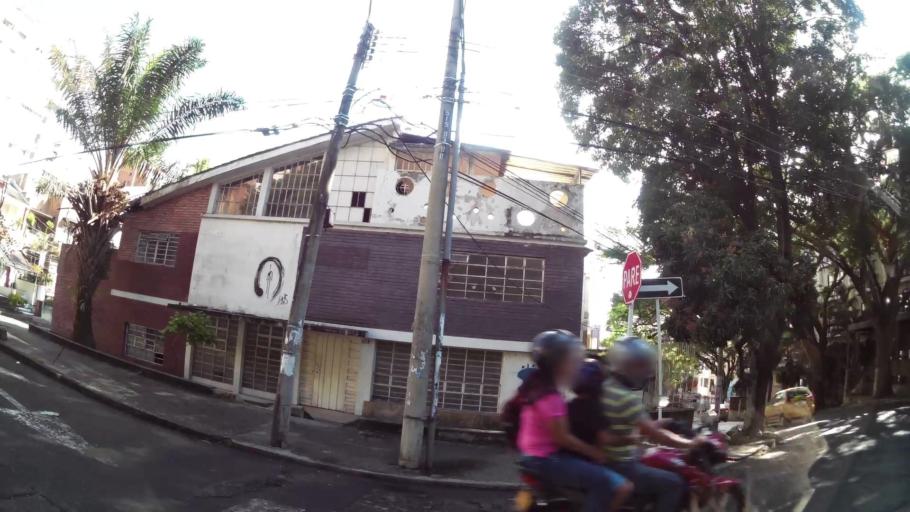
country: CO
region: Valle del Cauca
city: Cali
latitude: 3.4560
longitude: -76.5374
